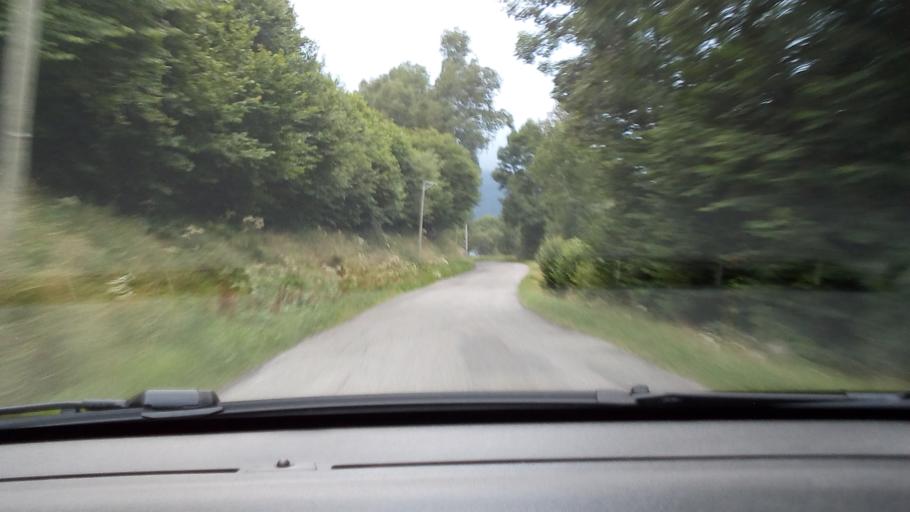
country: FR
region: Midi-Pyrenees
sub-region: Departement des Hautes-Pyrenees
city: Cauterets
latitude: 42.9527
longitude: -0.1982
